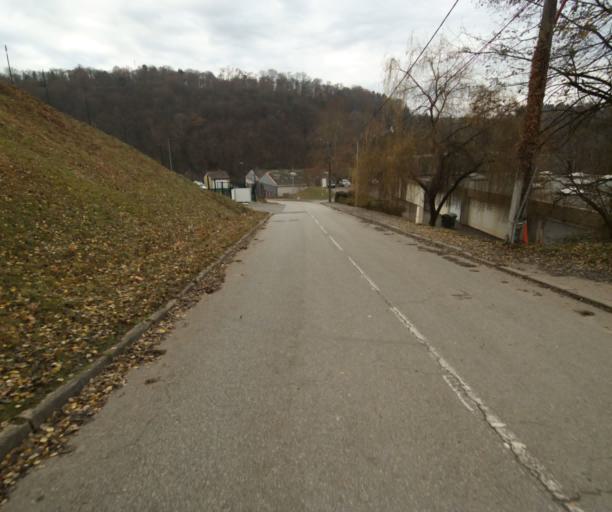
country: FR
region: Limousin
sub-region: Departement de la Correze
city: Tulle
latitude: 45.2419
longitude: 1.7378
